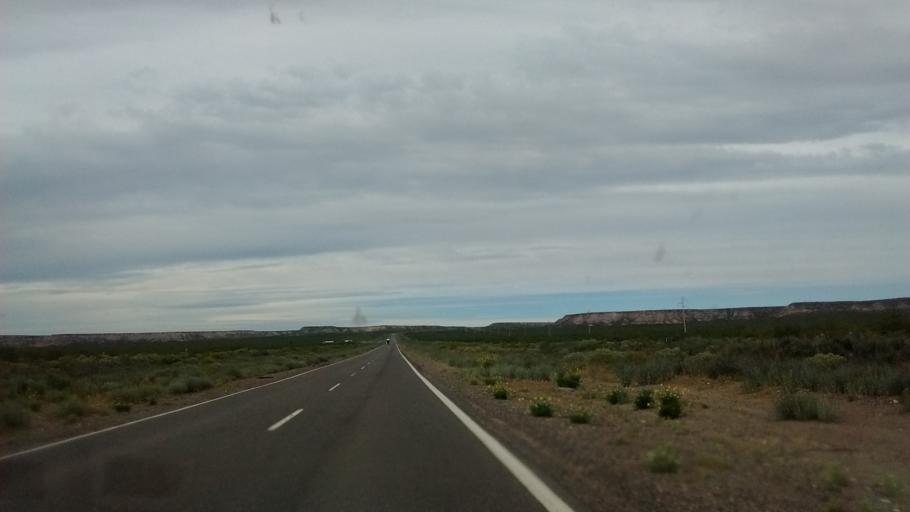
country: AR
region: Rio Negro
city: Catriel
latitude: -38.1694
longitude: -67.9519
